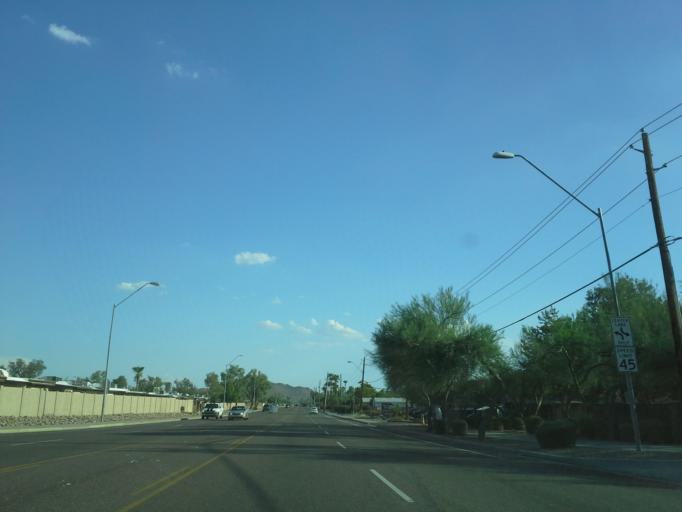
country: US
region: Arizona
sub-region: Maricopa County
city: Paradise Valley
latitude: 33.6528
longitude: -112.0309
